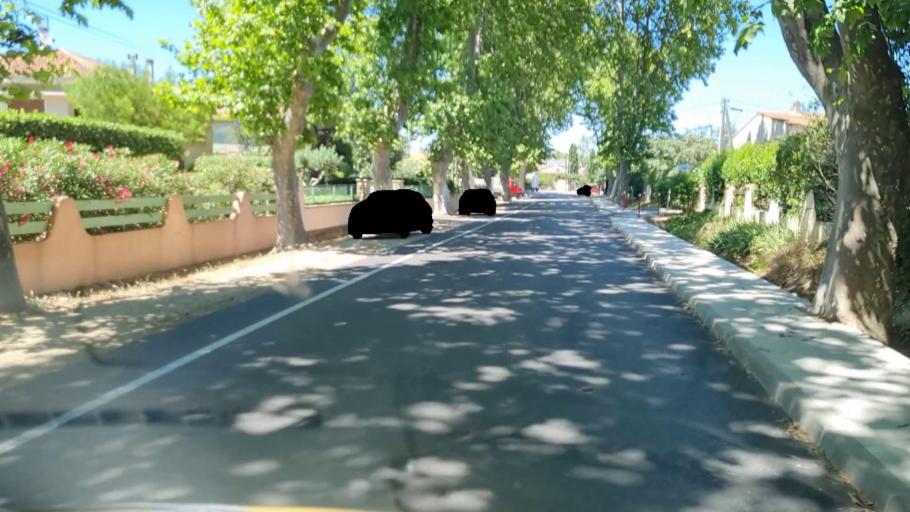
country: FR
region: Languedoc-Roussillon
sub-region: Departement du Gard
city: Le Cailar
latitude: 43.6790
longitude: 4.2354
